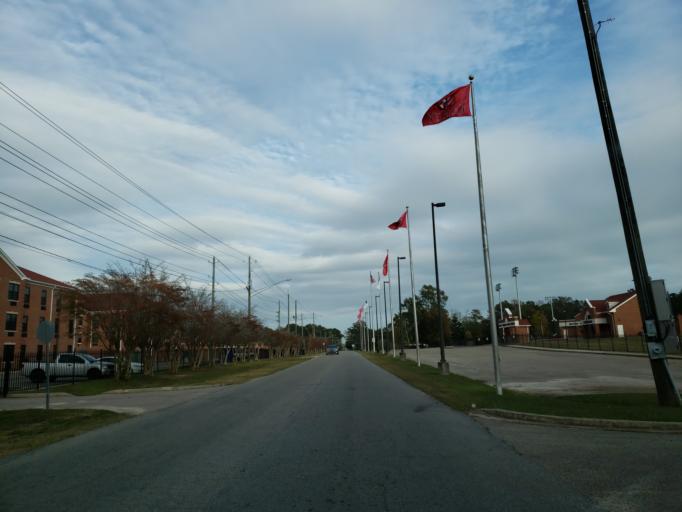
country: US
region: Mississippi
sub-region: Forrest County
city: Hattiesburg
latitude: 31.3028
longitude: -89.2936
